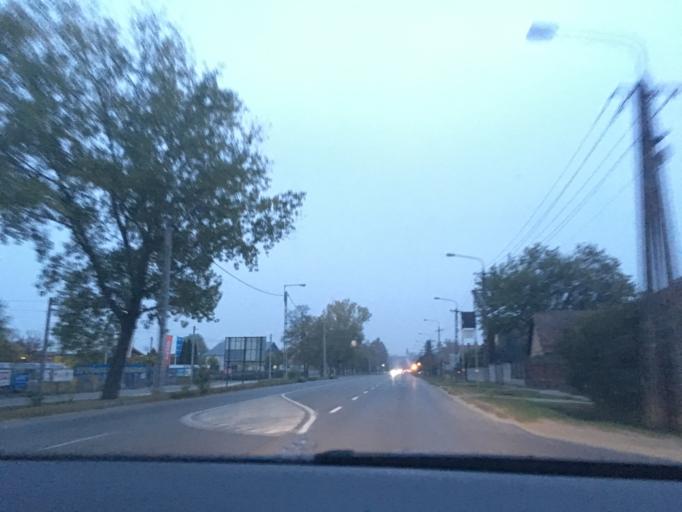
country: HU
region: Pest
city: Pilis
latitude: 47.2903
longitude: 19.5387
